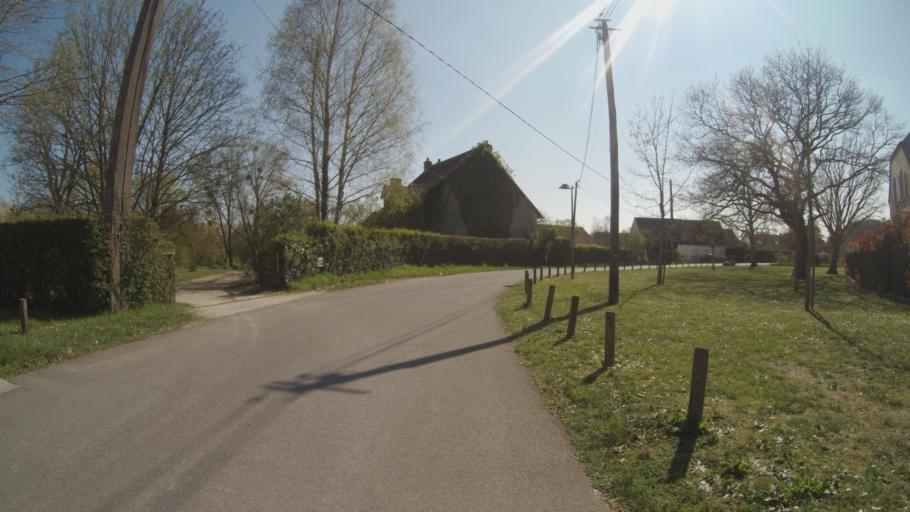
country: FR
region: Centre
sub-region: Departement du Loiret
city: Chanteau
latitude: 47.9628
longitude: 1.9670
